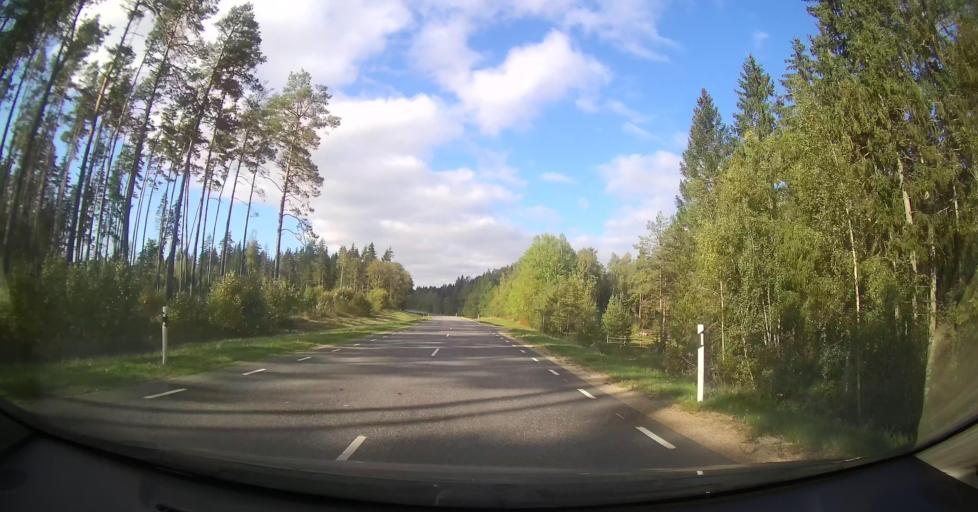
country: EE
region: Harju
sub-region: Anija vald
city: Kehra
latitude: 59.2219
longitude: 25.2508
